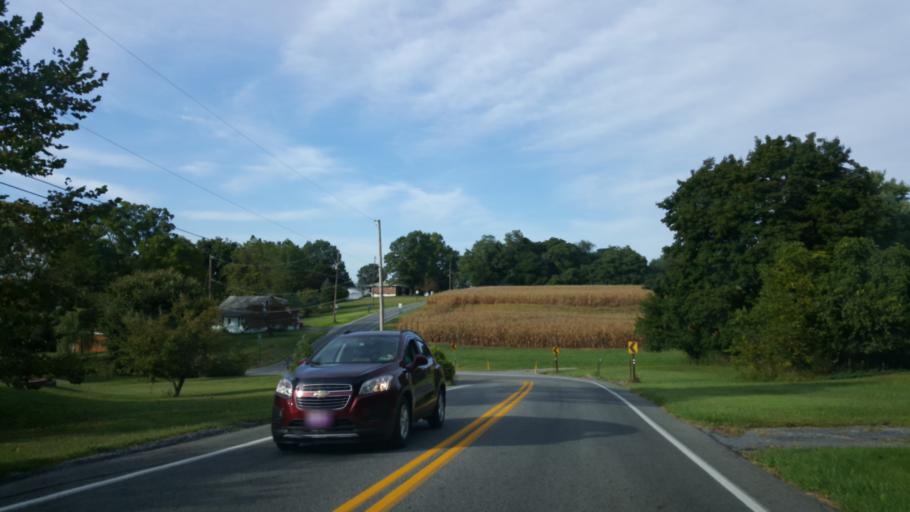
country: US
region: Pennsylvania
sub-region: Lebanon County
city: Campbelltown
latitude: 40.2601
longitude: -76.5722
